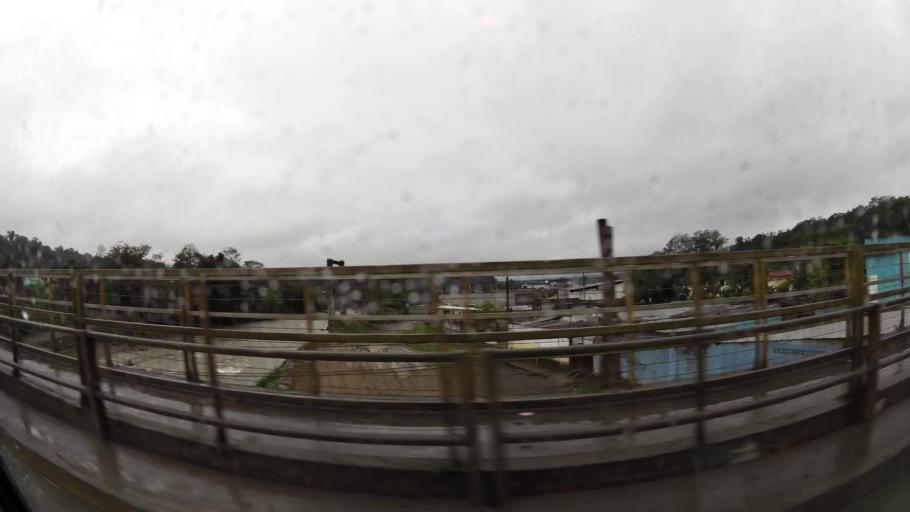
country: EC
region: Santo Domingo de los Tsachilas
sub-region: Canton Santo Domingo de los Colorados
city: Santo Domingo de los Colorados
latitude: -0.2439
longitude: -79.1369
